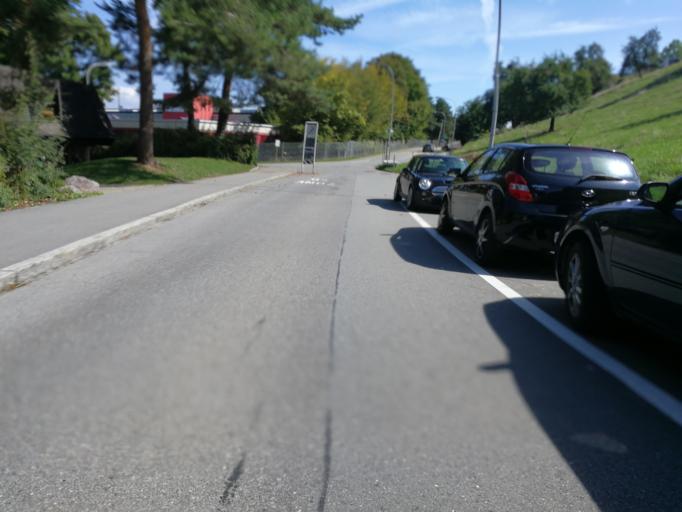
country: CH
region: Zurich
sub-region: Bezirk Horgen
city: Au / Mittel-Dorf
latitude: 47.2447
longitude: 8.6473
